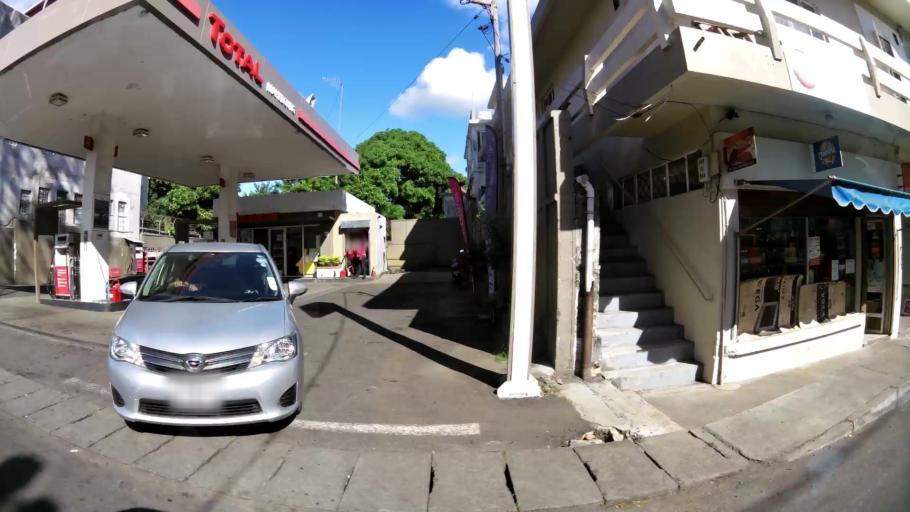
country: MU
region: Grand Port
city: Mahebourg
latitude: -20.4078
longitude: 57.7058
